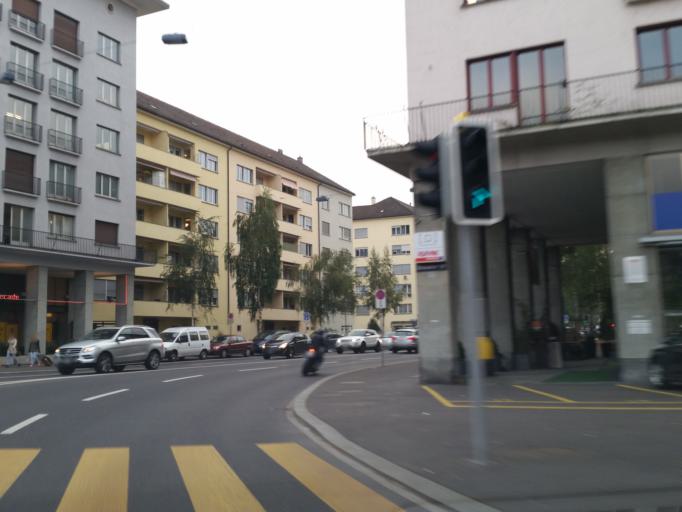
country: CH
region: Zurich
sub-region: Bezirk Zuerich
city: Zuerich (Kreis 4) / Werd
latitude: 47.3710
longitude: 8.5237
